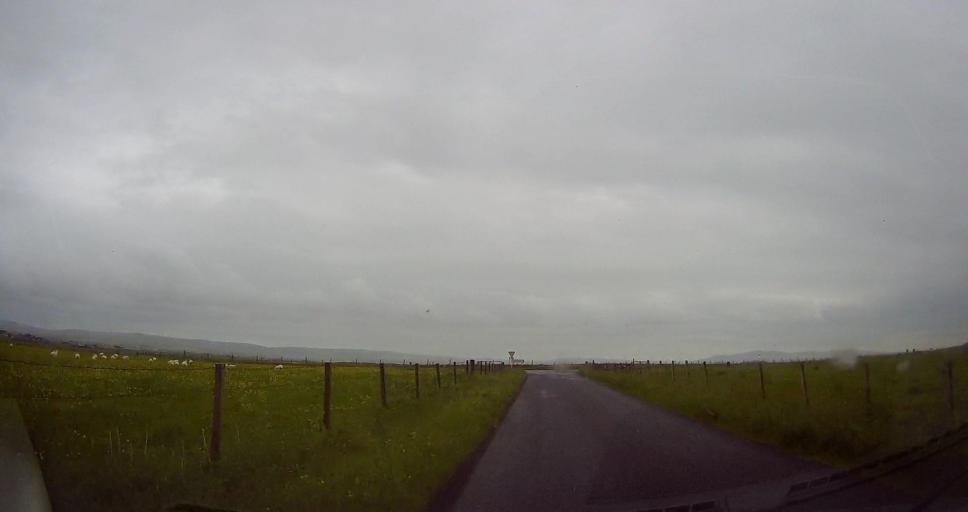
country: GB
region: Scotland
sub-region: Orkney Islands
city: Stromness
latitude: 59.0689
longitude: -3.2819
